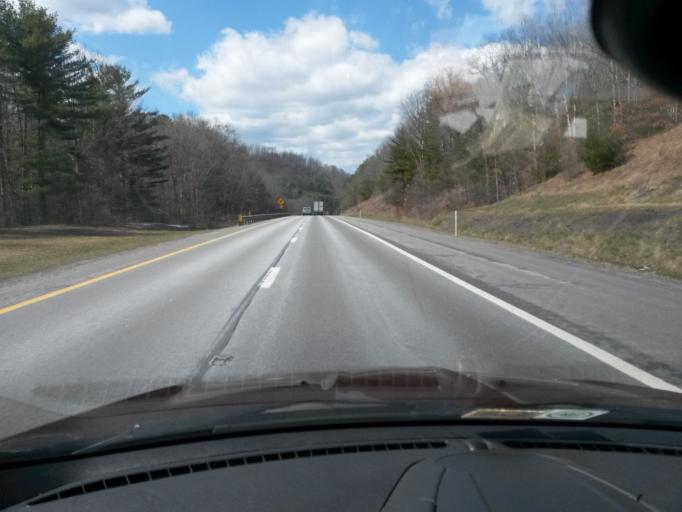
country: US
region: West Virginia
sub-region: Raleigh County
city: Beaver
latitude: 37.7064
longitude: -81.1465
